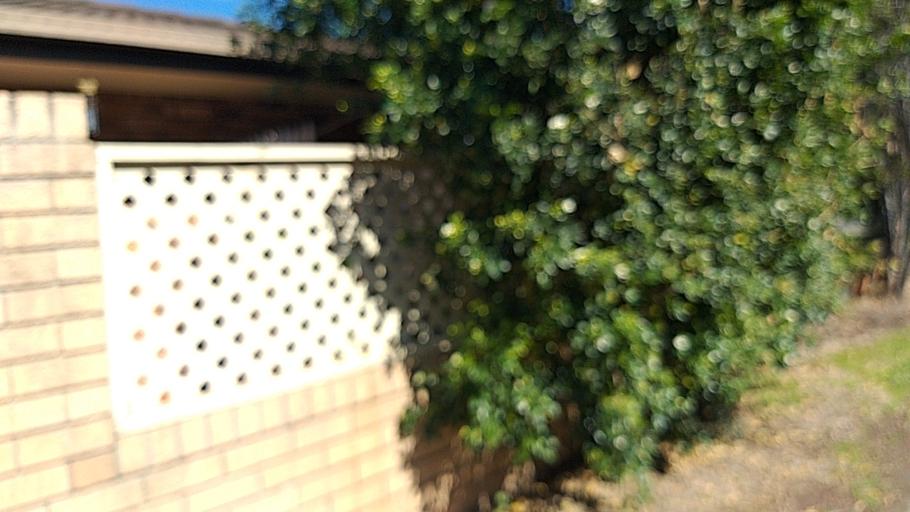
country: AU
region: New South Wales
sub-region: Wollongong
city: Dapto
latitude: -34.4884
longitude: 150.7793
